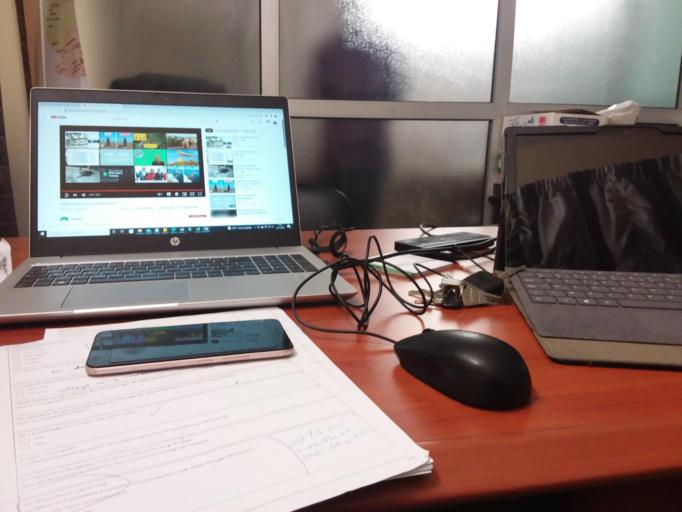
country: TG
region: Maritime
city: Lome
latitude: 6.1872
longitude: 1.1941
